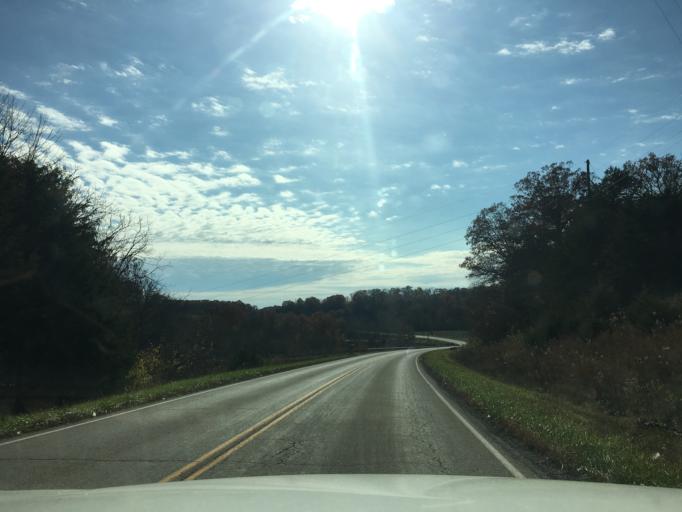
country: US
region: Missouri
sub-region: Osage County
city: Linn
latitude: 38.3987
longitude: -91.8212
